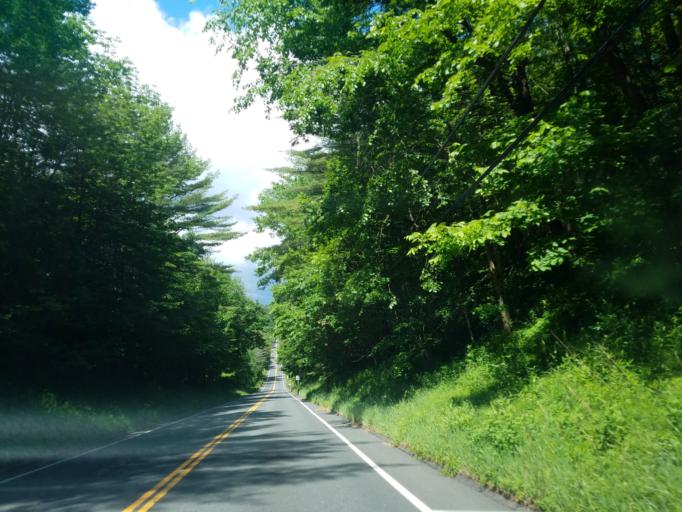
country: US
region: Connecticut
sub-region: Litchfield County
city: New Hartford Center
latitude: 41.9147
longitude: -72.9702
